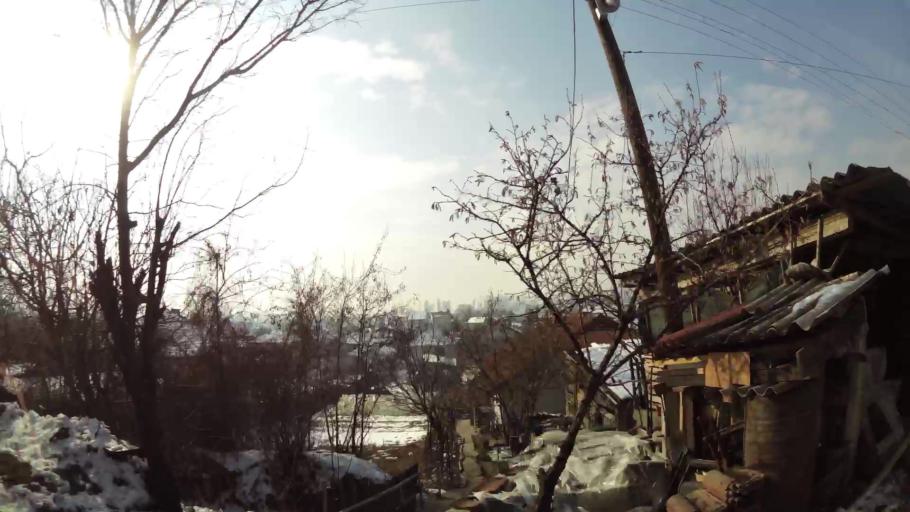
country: MK
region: Suto Orizari
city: Suto Orizare
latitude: 42.0269
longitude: 21.3782
